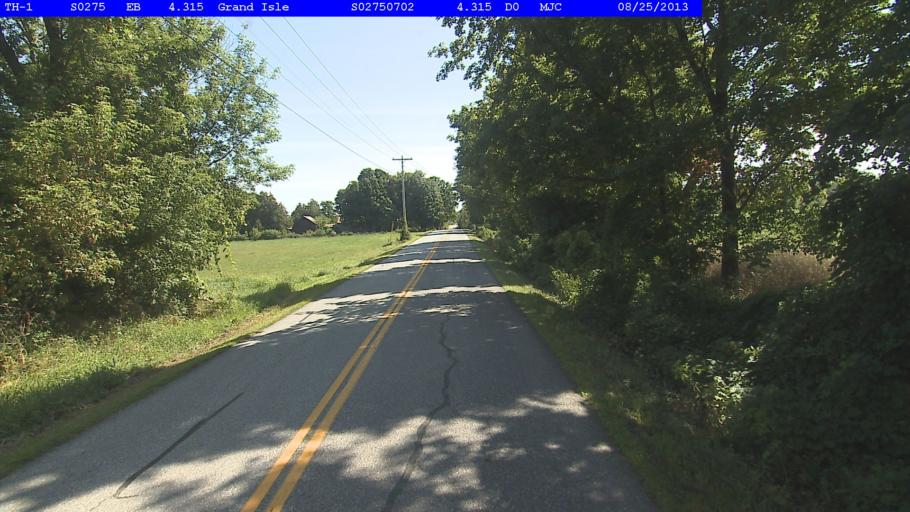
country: US
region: Vermont
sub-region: Grand Isle County
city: North Hero
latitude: 44.7407
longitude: -73.2972
